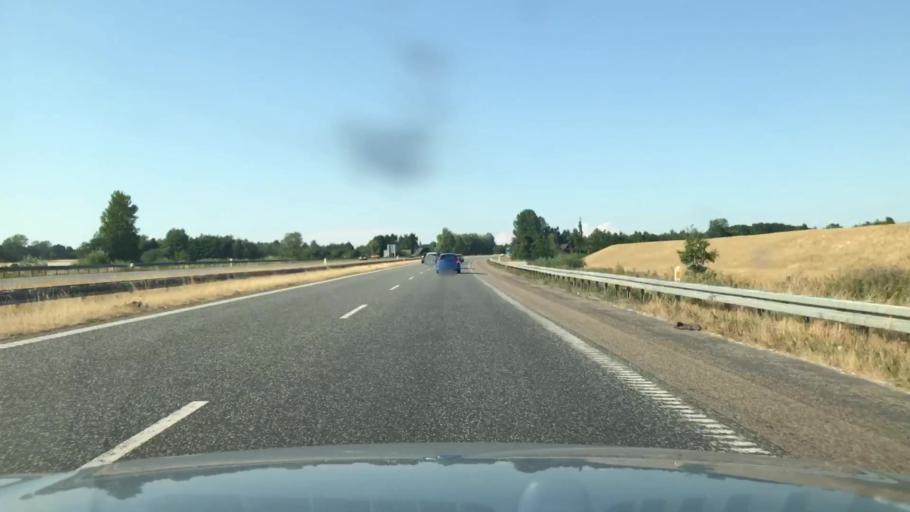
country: DK
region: Zealand
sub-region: Faxe Kommune
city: Ronnede
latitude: 55.2726
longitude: 12.0080
